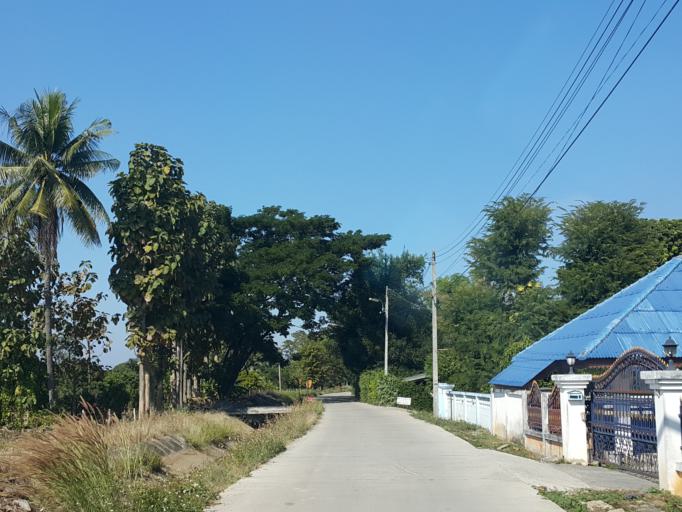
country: TH
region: Chiang Mai
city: San Sai
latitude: 18.8711
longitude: 98.9840
